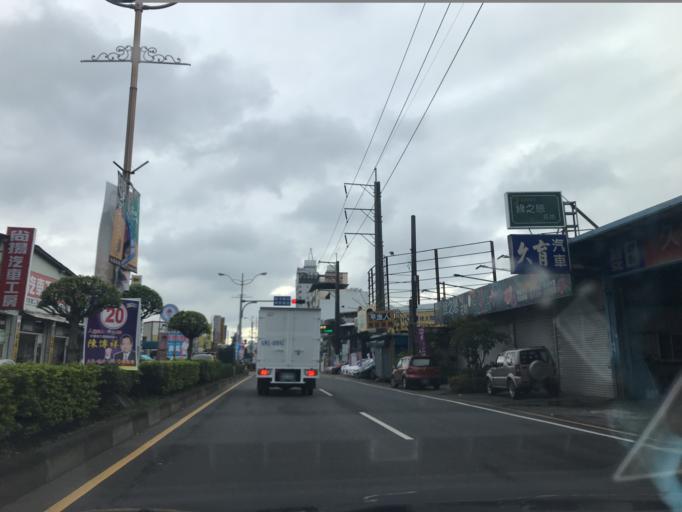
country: TW
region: Taiwan
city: Taoyuan City
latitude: 24.9560
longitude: 121.2467
